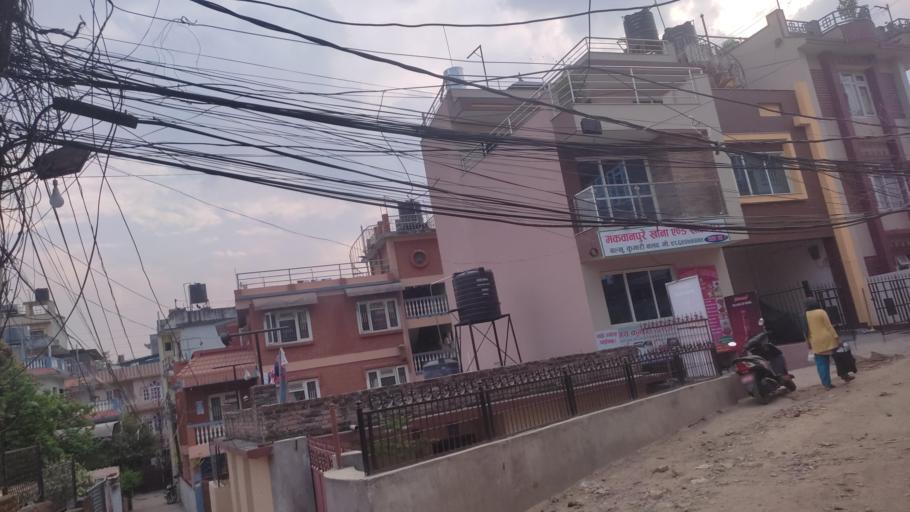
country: NP
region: Central Region
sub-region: Bagmati Zone
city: Patan
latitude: 27.6819
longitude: 85.2973
